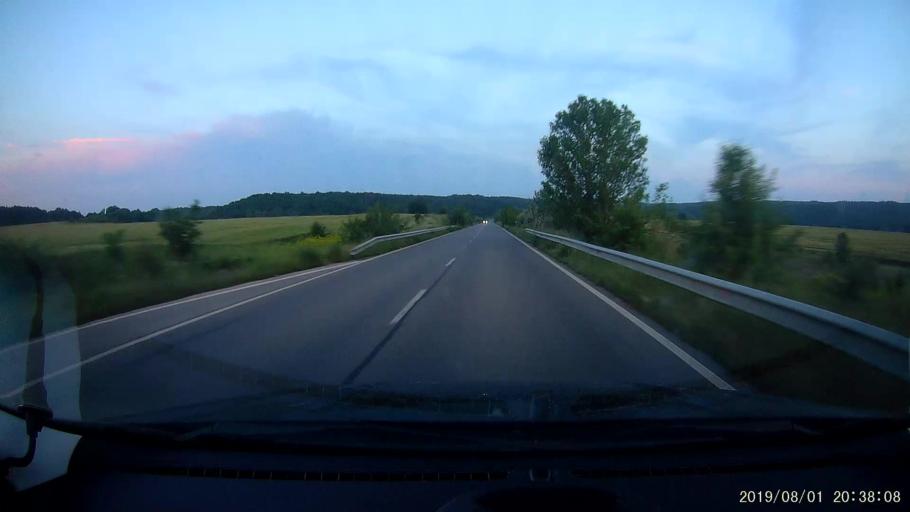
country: BG
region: Yambol
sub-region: Obshtina Elkhovo
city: Elkhovo
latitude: 42.0329
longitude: 26.5986
